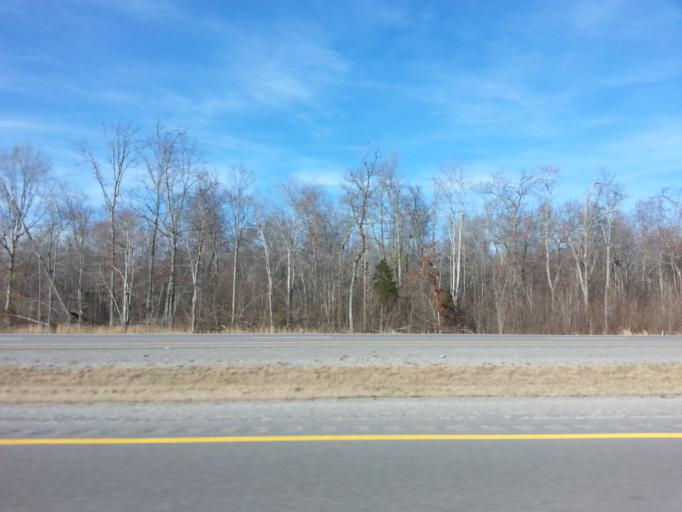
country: US
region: Tennessee
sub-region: Warren County
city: McMinnville
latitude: 35.7161
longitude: -85.8606
